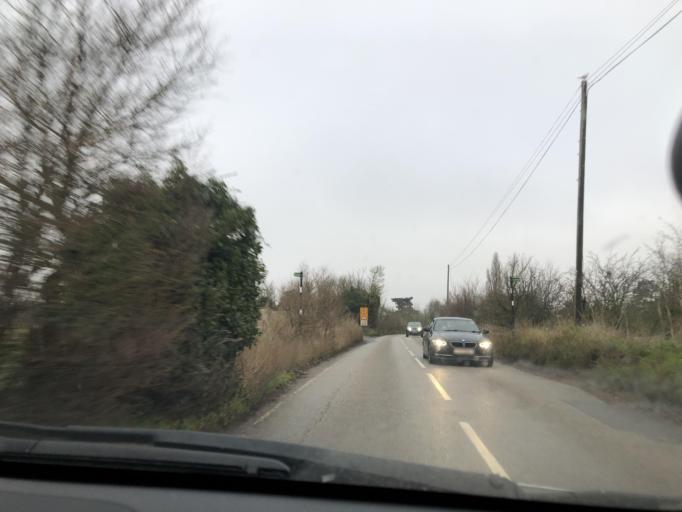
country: GB
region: England
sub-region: Kent
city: Longfield
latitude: 51.4149
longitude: 0.3291
